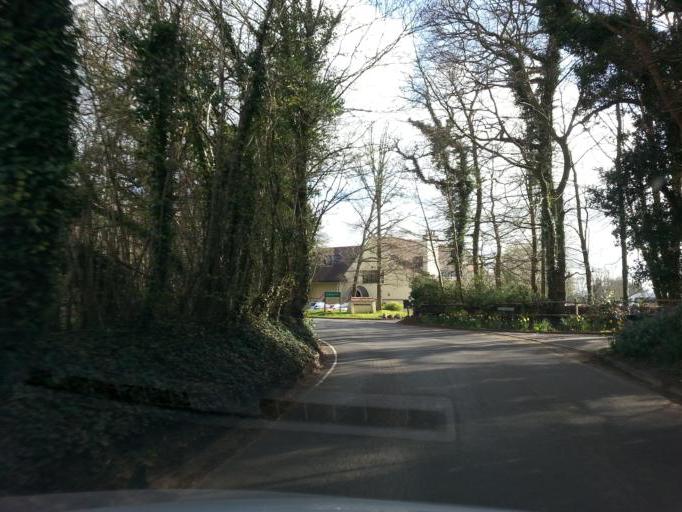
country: GB
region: England
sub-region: Surrey
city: Godalming
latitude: 51.2086
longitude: -0.6419
